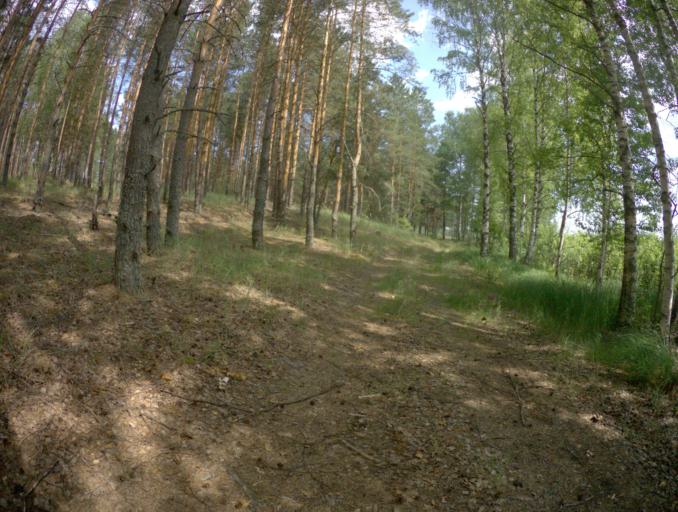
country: RU
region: Ivanovo
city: Talitsy
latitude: 56.3894
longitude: 42.3364
